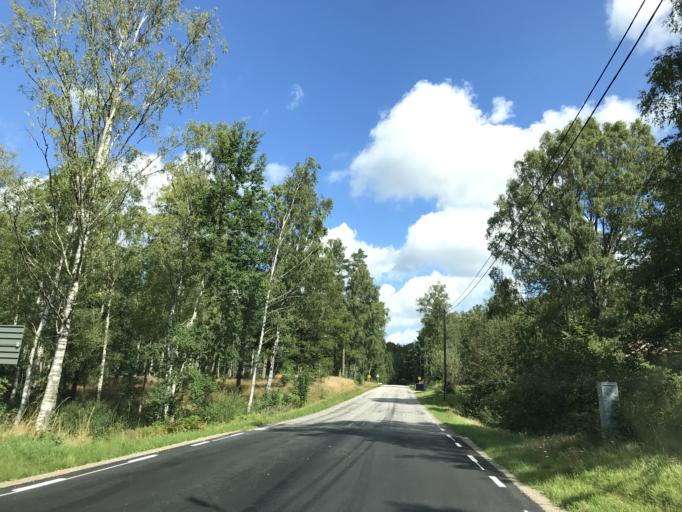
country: SE
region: Halland
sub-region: Laholms Kommun
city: Knared
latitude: 56.4306
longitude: 13.3069
